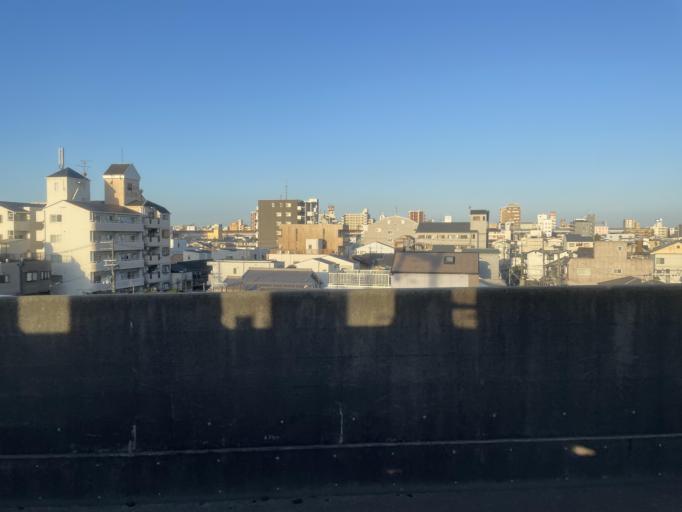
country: JP
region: Osaka
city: Matsubara
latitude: 34.6286
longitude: 135.5302
